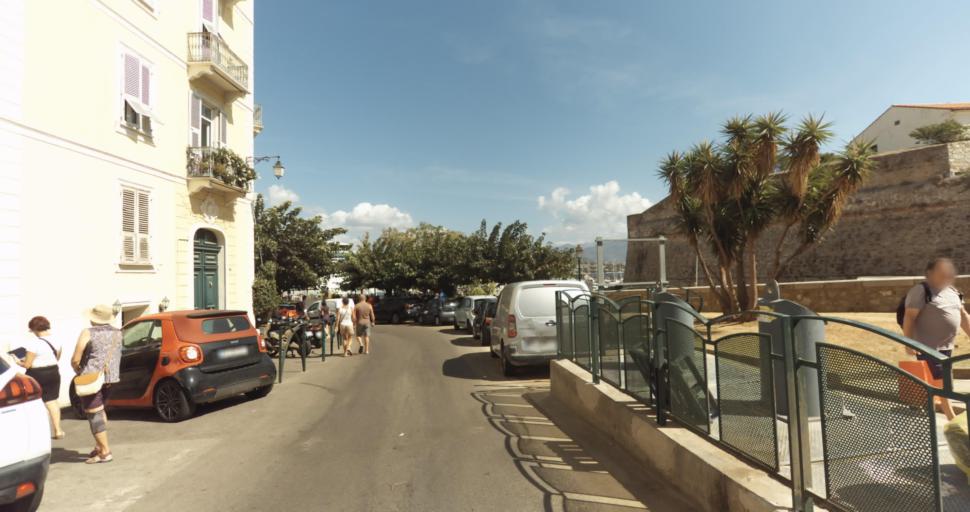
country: FR
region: Corsica
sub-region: Departement de la Corse-du-Sud
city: Ajaccio
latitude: 41.9176
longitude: 8.7398
